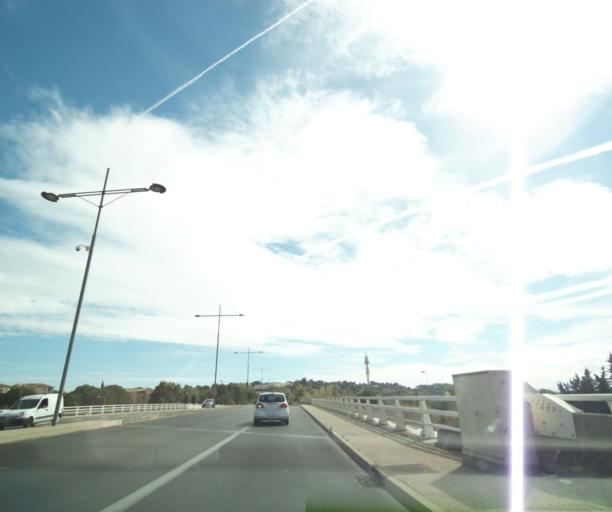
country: FR
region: Languedoc-Roussillon
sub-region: Departement de l'Herault
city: Juvignac
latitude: 43.6157
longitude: 3.8205
